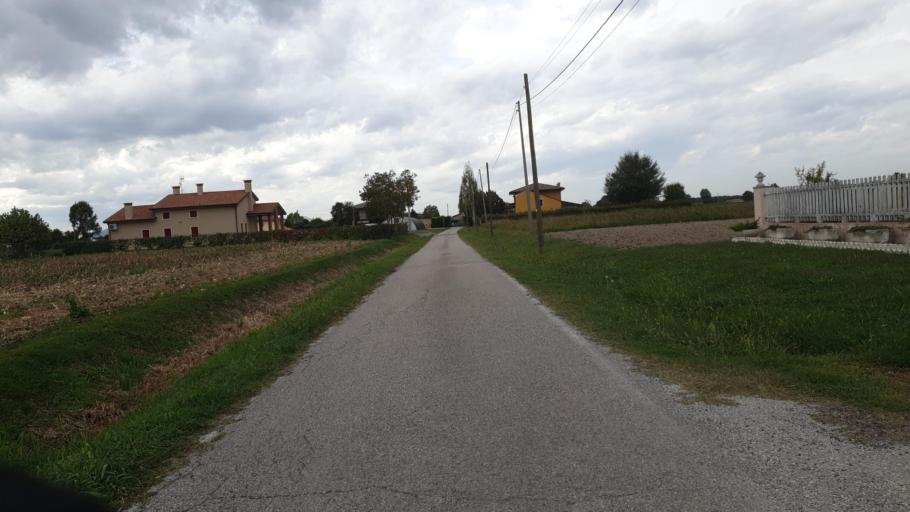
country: IT
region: Veneto
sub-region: Provincia di Padova
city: Bovolenta
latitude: 45.2829
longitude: 11.9478
